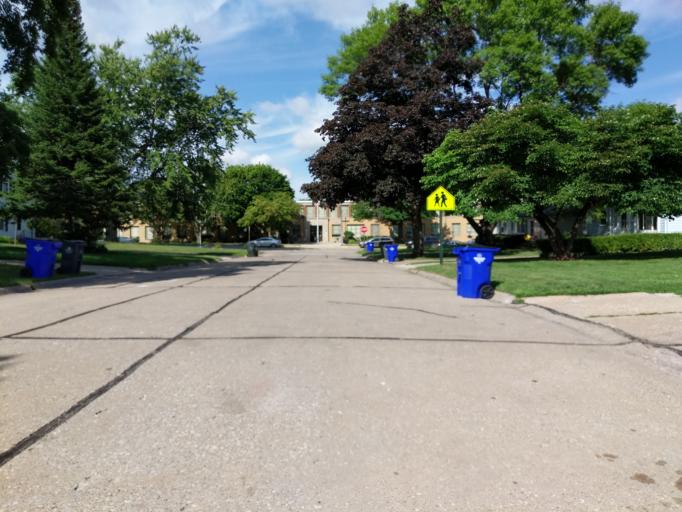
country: US
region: Iowa
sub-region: Linn County
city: Cedar Rapids
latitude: 42.0160
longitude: -91.6401
